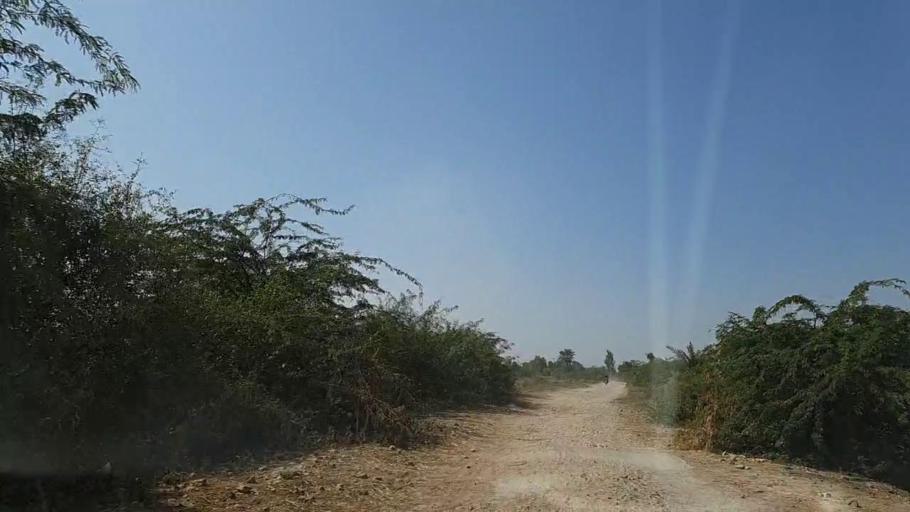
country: PK
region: Sindh
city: Chuhar Jamali
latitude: 24.4242
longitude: 68.0058
